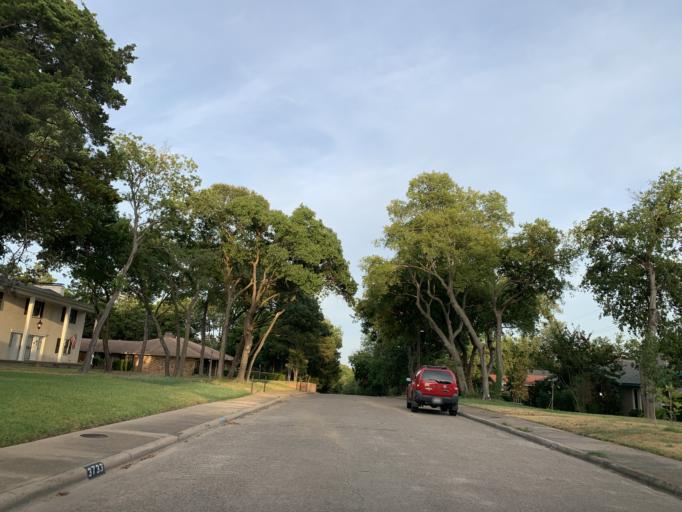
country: US
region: Texas
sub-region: Dallas County
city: Cockrell Hill
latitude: 32.7026
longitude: -96.8821
